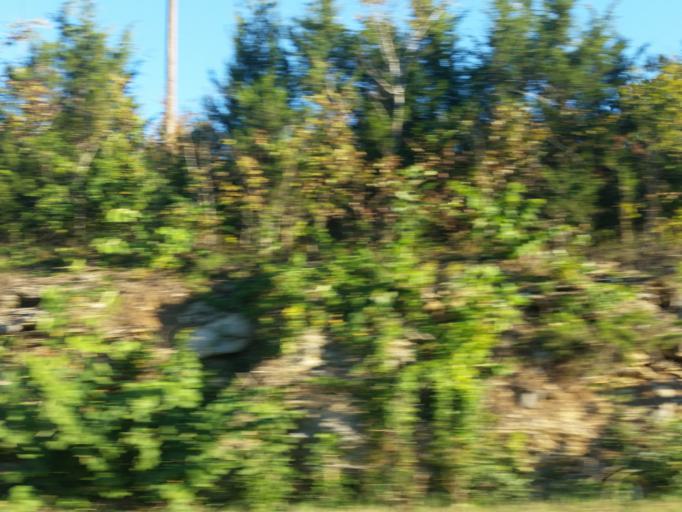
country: US
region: Tennessee
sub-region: Grainger County
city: Bean Station
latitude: 36.3645
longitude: -83.4061
